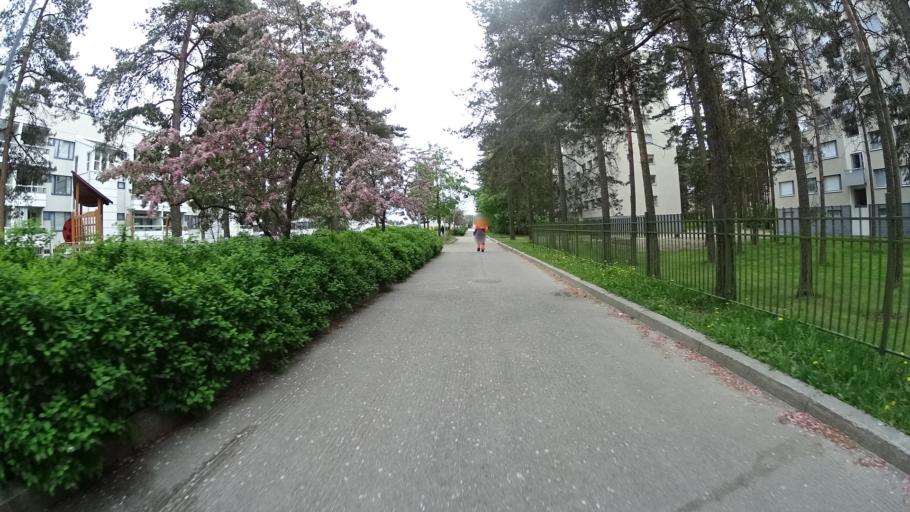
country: FI
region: Uusimaa
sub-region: Helsinki
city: Vantaa
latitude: 60.2391
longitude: 25.0813
